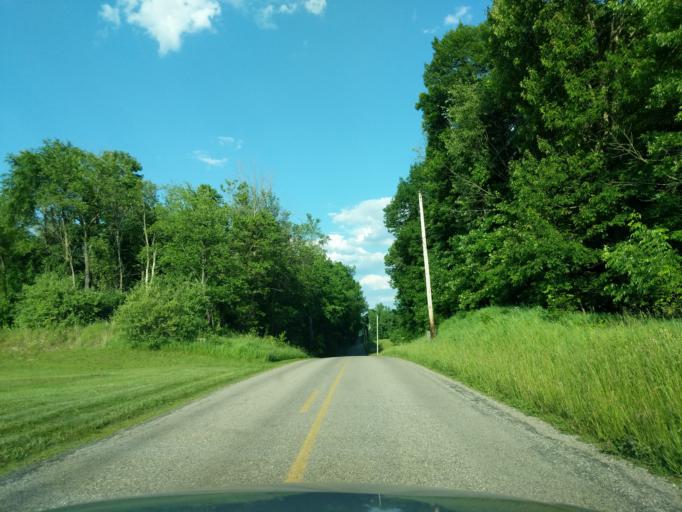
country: US
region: Indiana
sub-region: Kosciusko County
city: North Webster
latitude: 41.3026
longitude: -85.5719
